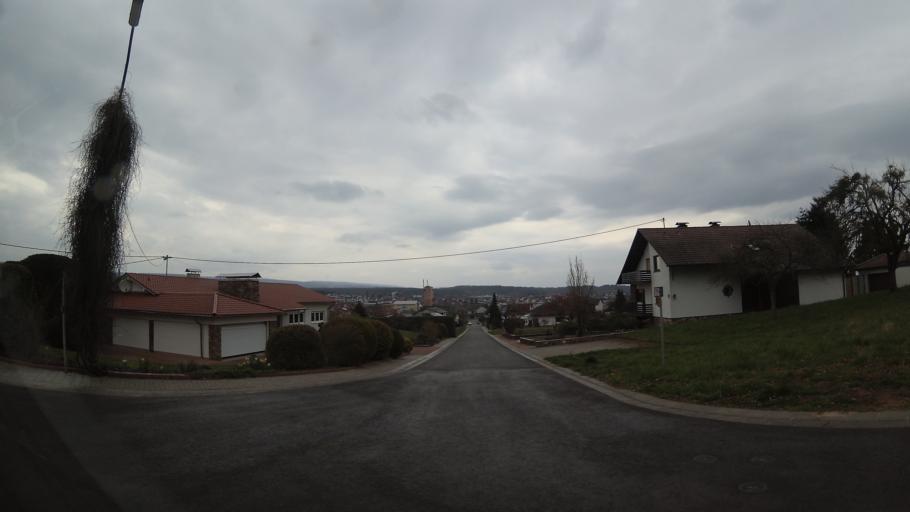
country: DE
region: Saarland
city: Losheim
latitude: 49.5033
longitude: 6.7415
